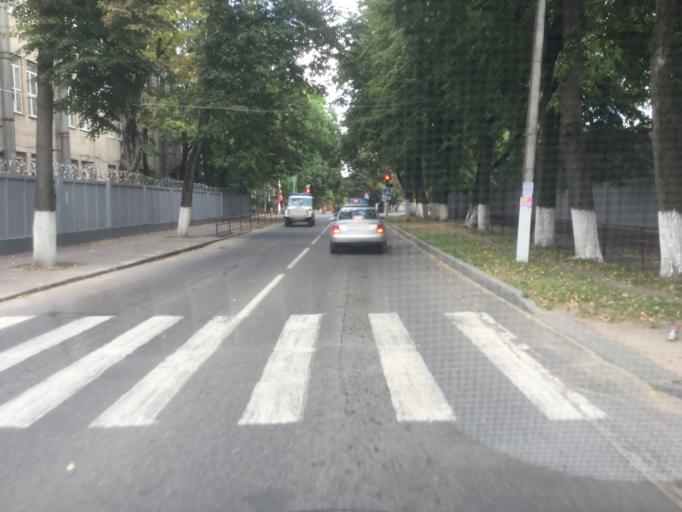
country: BY
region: Vitebsk
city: Vitebsk
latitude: 55.1962
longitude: 30.1943
